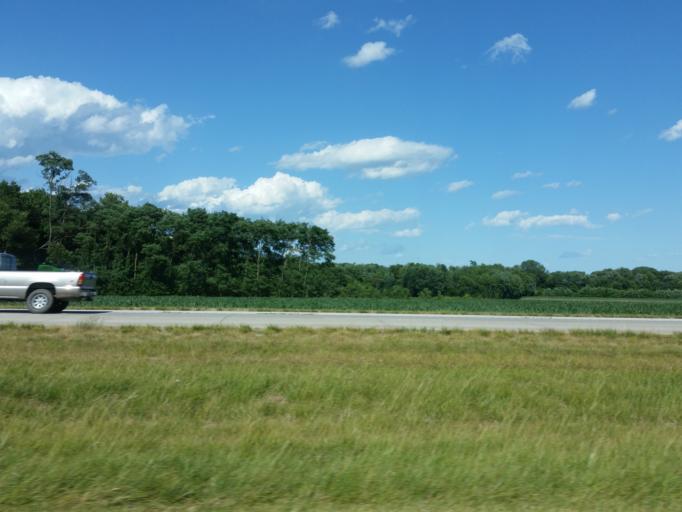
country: US
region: Missouri
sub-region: Lewis County
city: Canton
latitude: 40.1985
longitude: -91.5225
